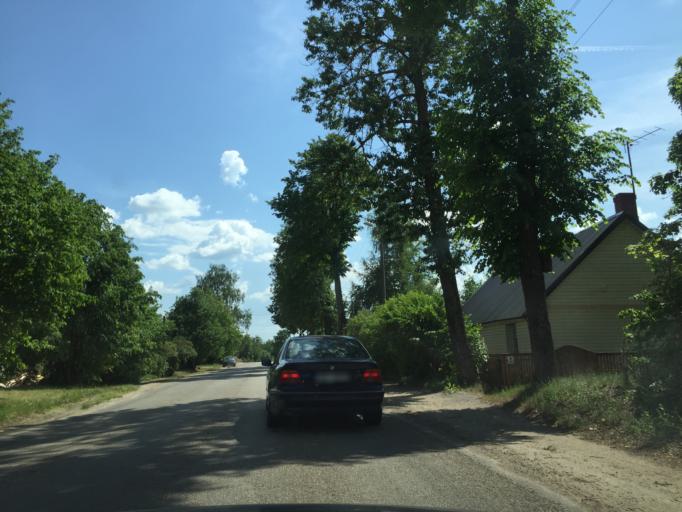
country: LV
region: Rezekne
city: Rezekne
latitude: 56.5317
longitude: 27.3131
